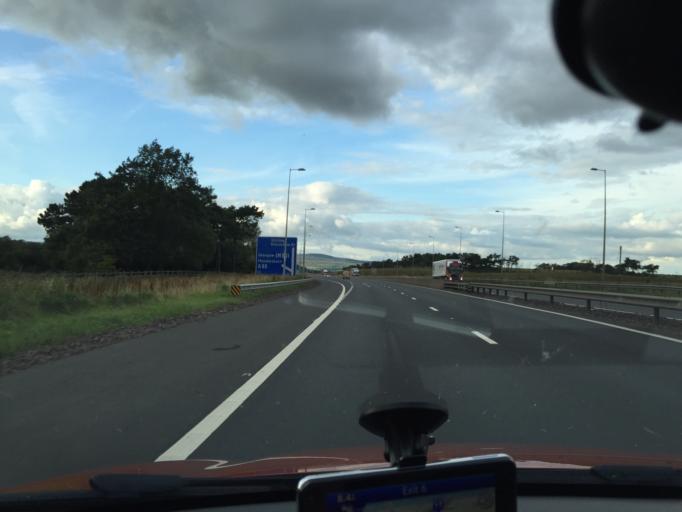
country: GB
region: Scotland
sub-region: North Lanarkshire
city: Glenboig
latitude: 55.9102
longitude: -4.0658
